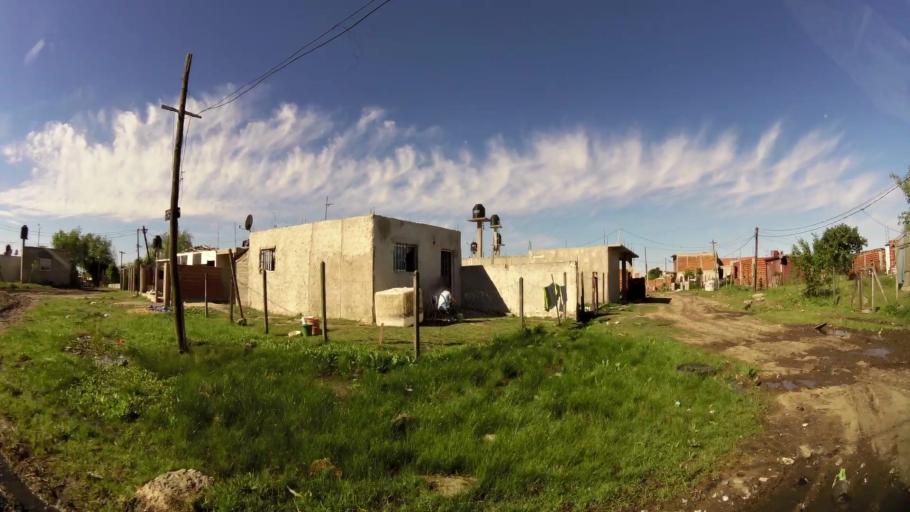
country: AR
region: Buenos Aires
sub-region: Partido de Quilmes
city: Quilmes
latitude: -34.7614
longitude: -58.3103
